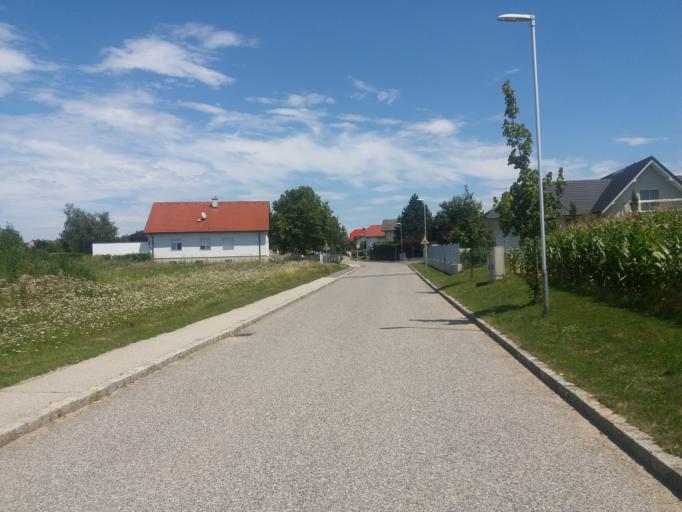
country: AT
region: Burgenland
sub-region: Politischer Bezirk Oberpullendorf
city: Raiding
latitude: 47.5661
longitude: 16.5334
